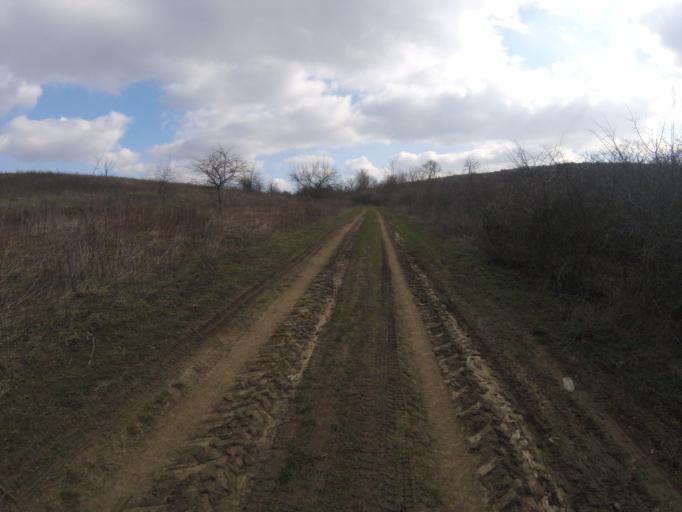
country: HU
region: Komarom-Esztergom
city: Nyergesujfalu
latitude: 47.7415
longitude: 18.5819
